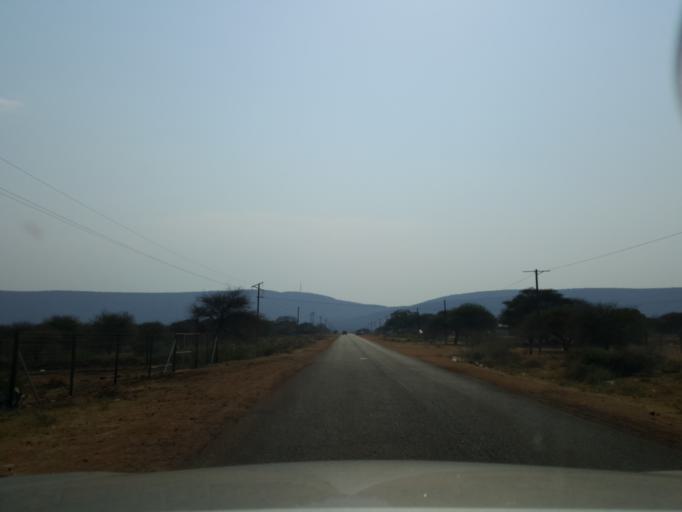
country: BW
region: South East
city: Lobatse
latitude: -25.3003
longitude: 25.8333
